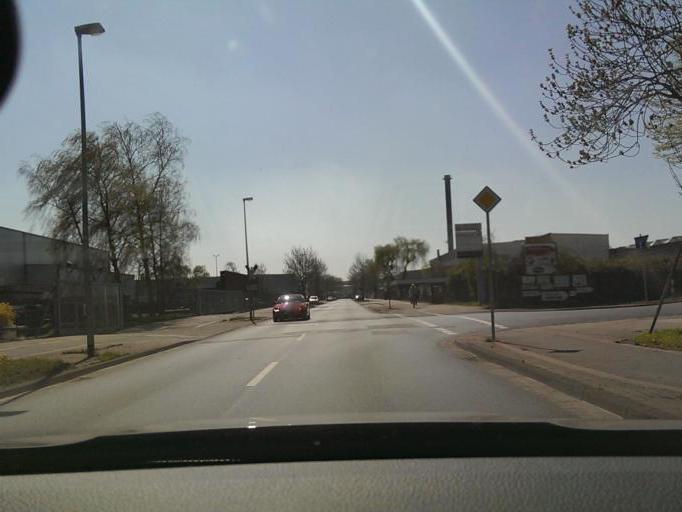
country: DE
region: Lower Saxony
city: Langenhagen
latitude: 52.4206
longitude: 9.7223
